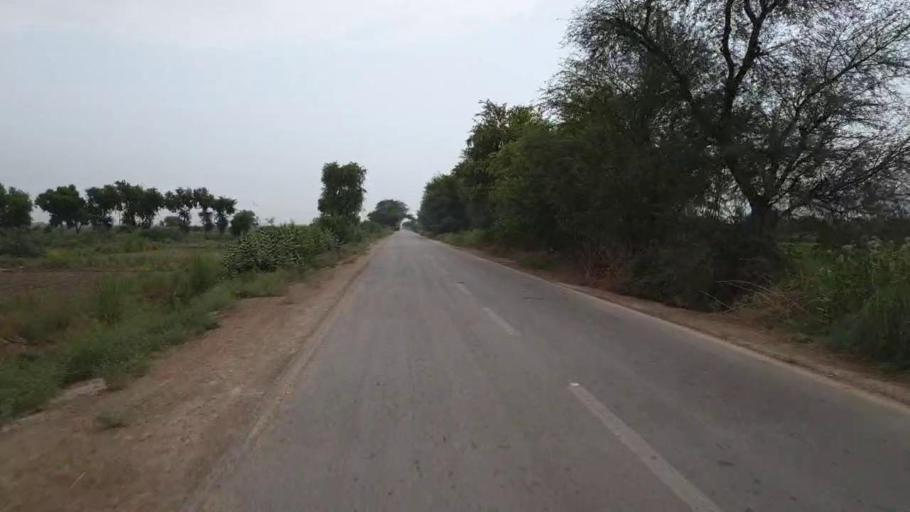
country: PK
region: Sindh
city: Bandhi
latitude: 26.5890
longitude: 68.2176
